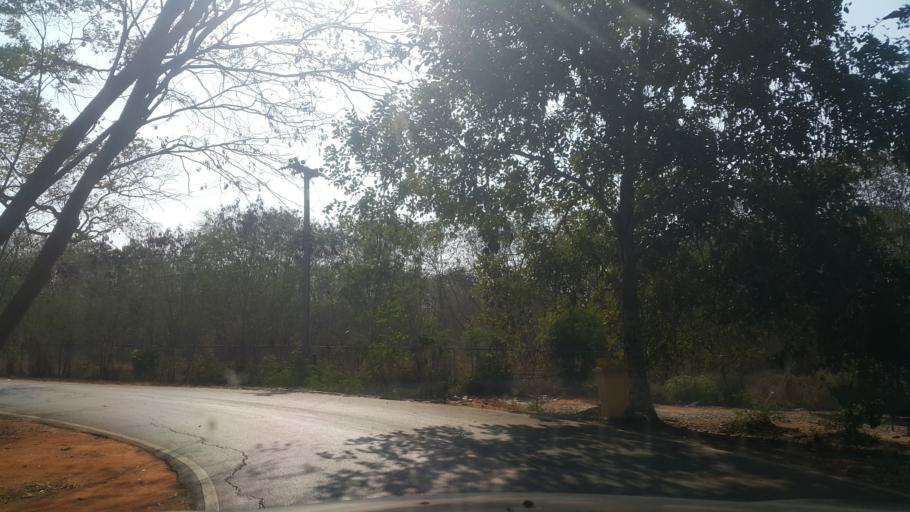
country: TH
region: Nakhon Ratchasima
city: Nakhon Ratchasima
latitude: 14.8568
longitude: 102.0858
